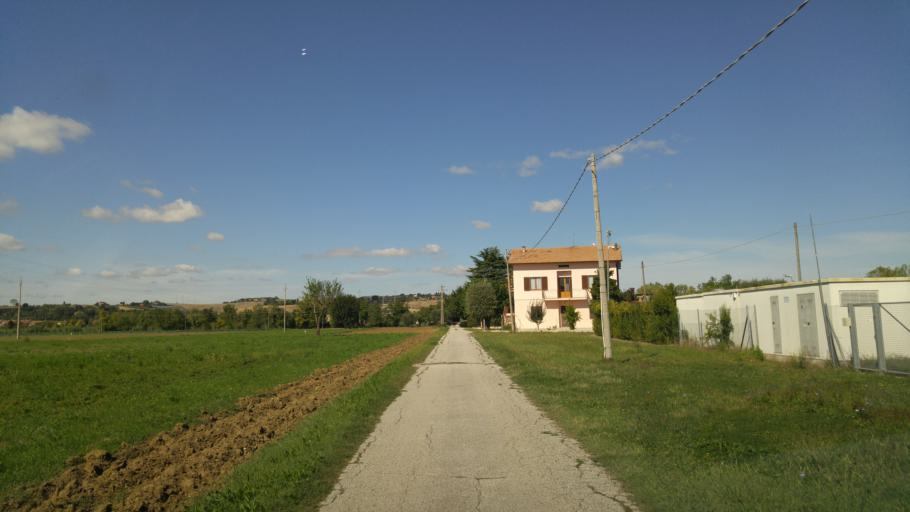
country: IT
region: The Marches
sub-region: Provincia di Pesaro e Urbino
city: Cuccurano
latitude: 43.7773
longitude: 12.9573
